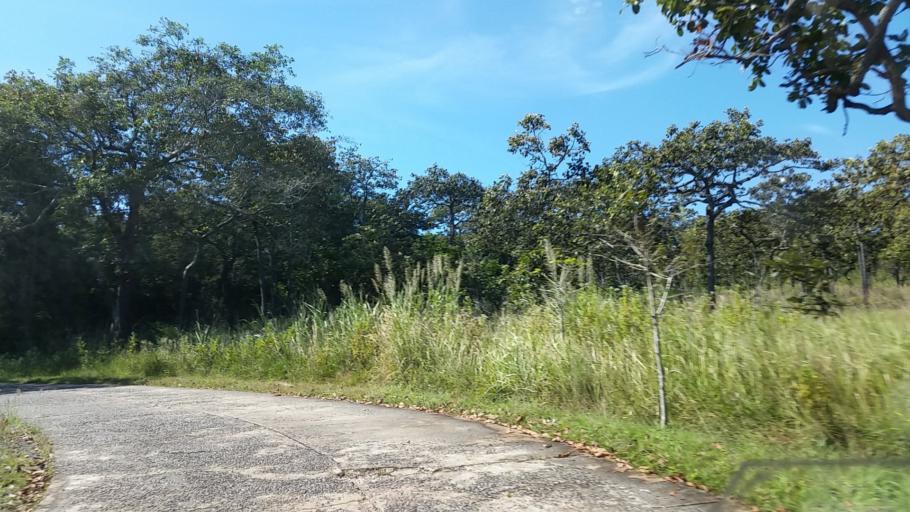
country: TH
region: Chaiyaphum
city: Sap Yai
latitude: 15.6333
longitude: 101.3907
